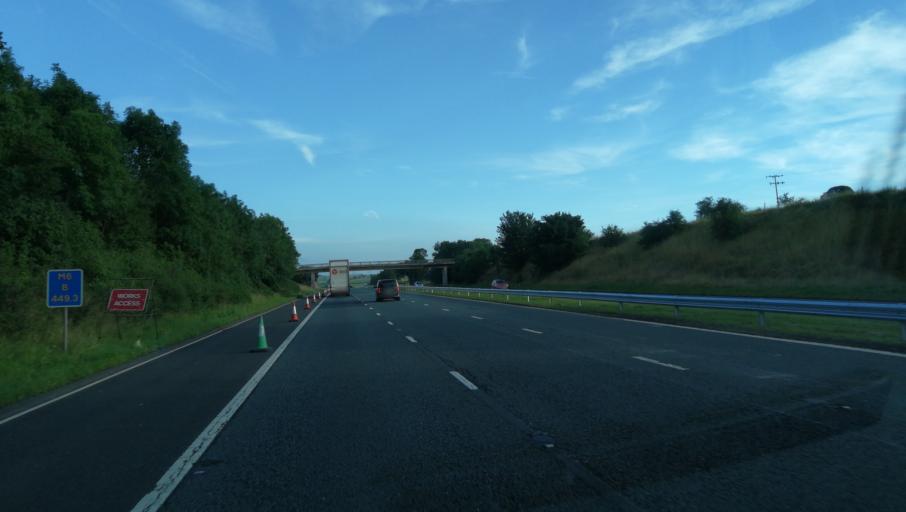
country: GB
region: England
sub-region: Cumbria
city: Penrith
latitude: 54.5750
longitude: -2.6935
